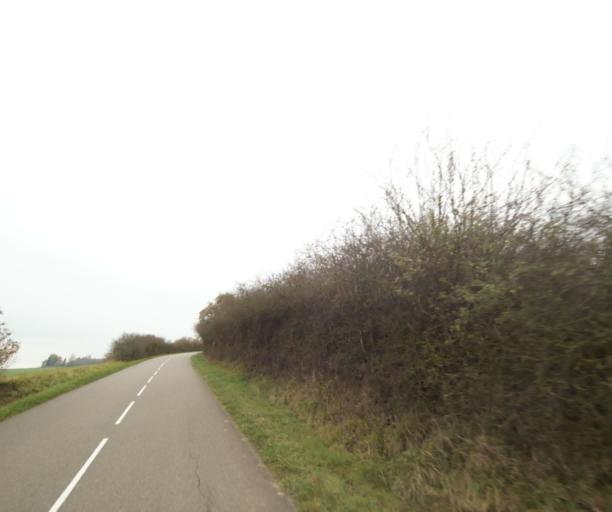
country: FR
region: Lorraine
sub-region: Departement de Meurthe-et-Moselle
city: Mancieulles
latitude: 49.2803
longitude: 5.8836
